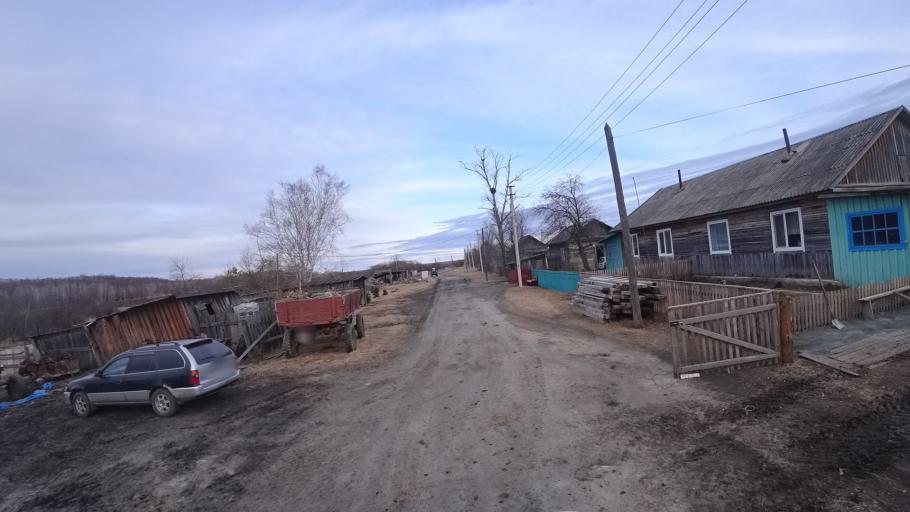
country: RU
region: Amur
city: Bureya
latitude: 50.0220
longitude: 129.7679
